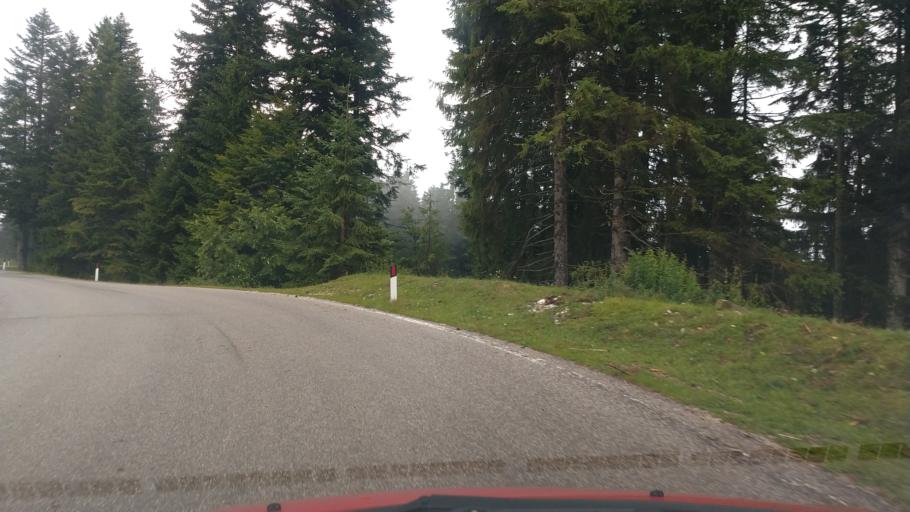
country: IT
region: Veneto
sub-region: Provincia di Vicenza
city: Lastebasse
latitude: 45.9102
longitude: 11.2406
